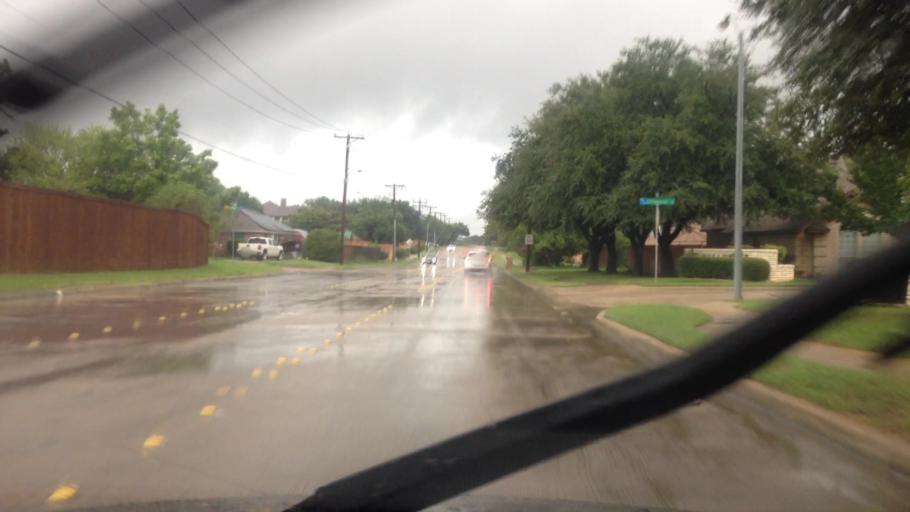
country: US
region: Texas
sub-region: Tarrant County
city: Watauga
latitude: 32.8821
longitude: -97.2195
